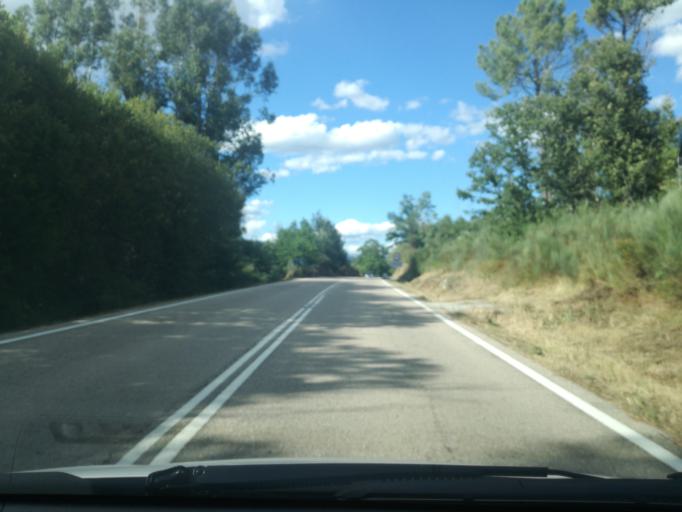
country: ES
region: Galicia
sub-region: Provincia de Ourense
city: Lobios
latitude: 41.8901
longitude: -8.0894
